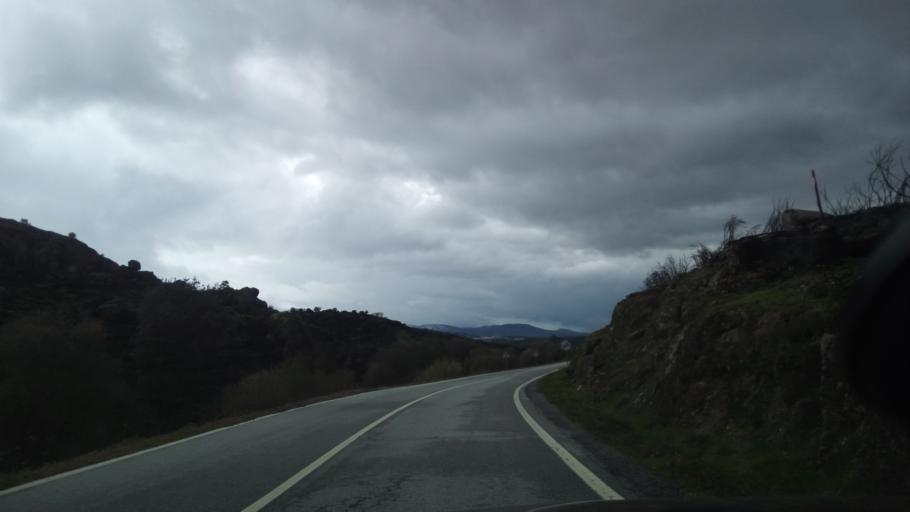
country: PT
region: Guarda
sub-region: Fornos de Algodres
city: Fornos de Algodres
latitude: 40.5659
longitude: -7.5568
